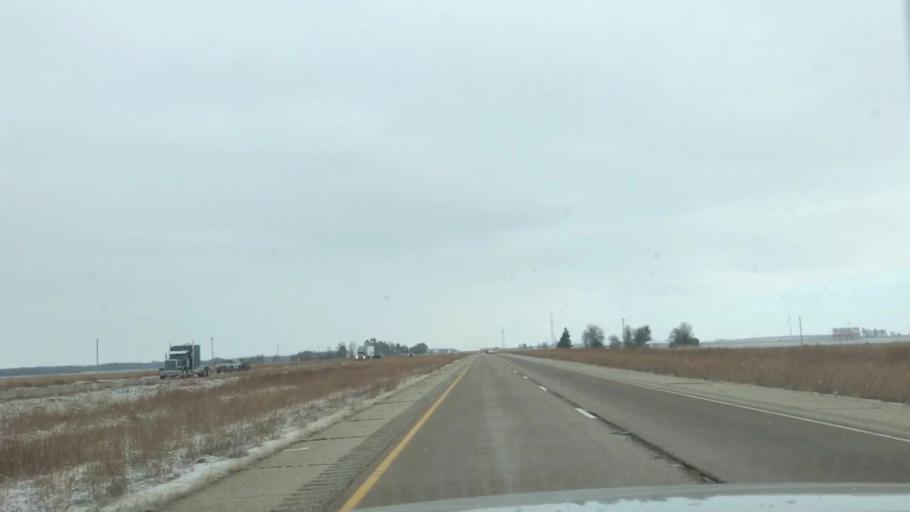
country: US
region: Illinois
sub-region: Montgomery County
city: Raymond
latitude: 39.4049
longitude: -89.6431
